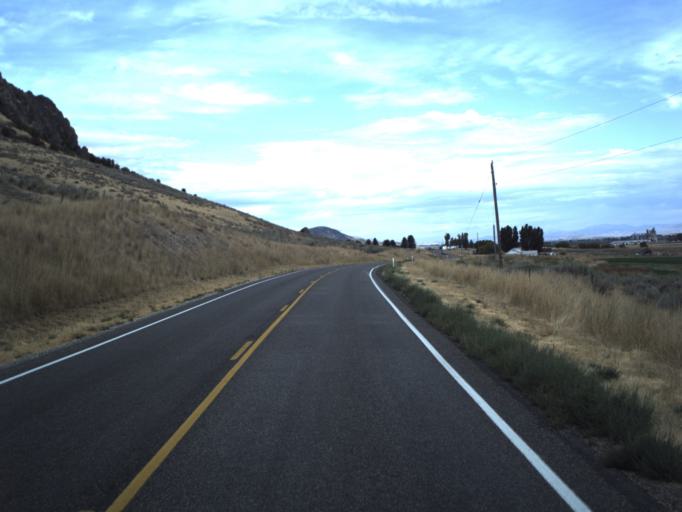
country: US
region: Utah
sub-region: Cache County
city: Benson
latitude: 41.8977
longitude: -111.9504
